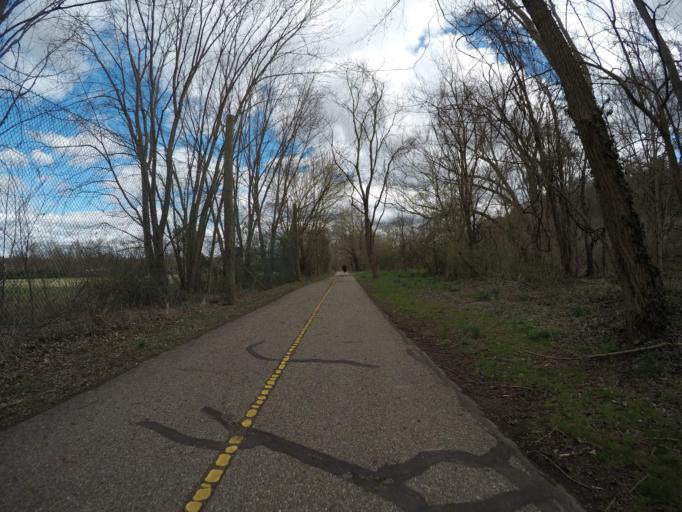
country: US
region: Ohio
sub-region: Washington County
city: Marietta
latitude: 39.4247
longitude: -81.4710
